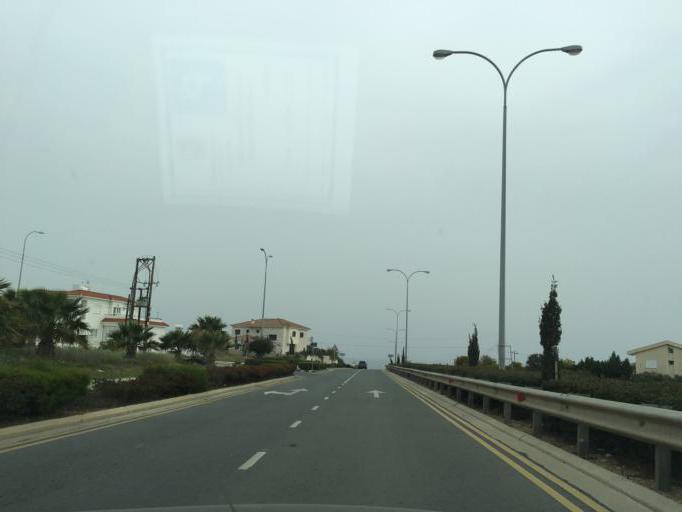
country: CY
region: Ammochostos
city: Ayia Napa
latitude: 35.0006
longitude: 33.9996
